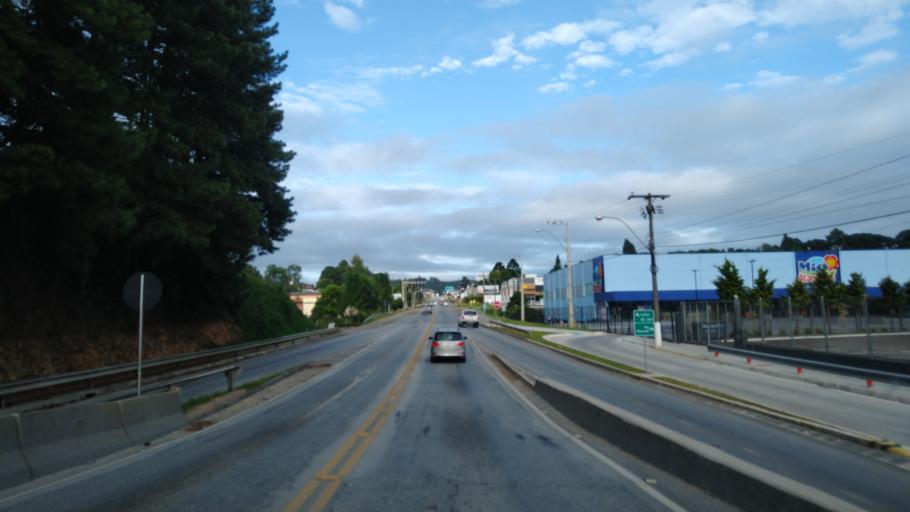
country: BR
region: Santa Catarina
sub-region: Sao Bento Do Sul
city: Sao Bento do Sul
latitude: -26.2240
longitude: -49.4022
